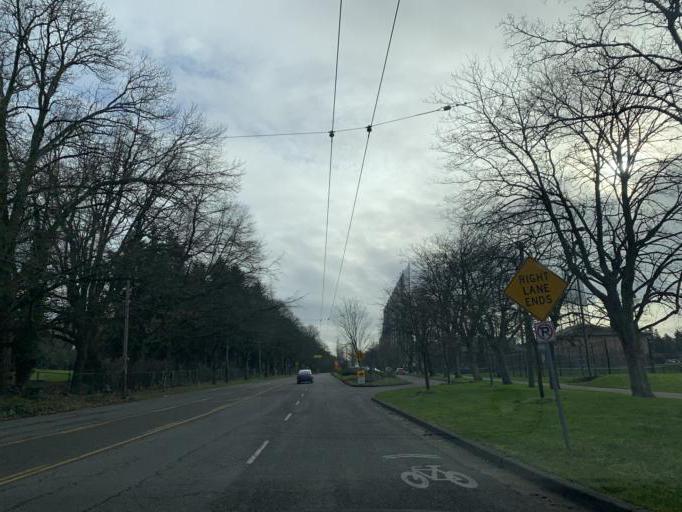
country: US
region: Washington
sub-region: King County
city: Seattle
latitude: 47.5713
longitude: -122.3081
